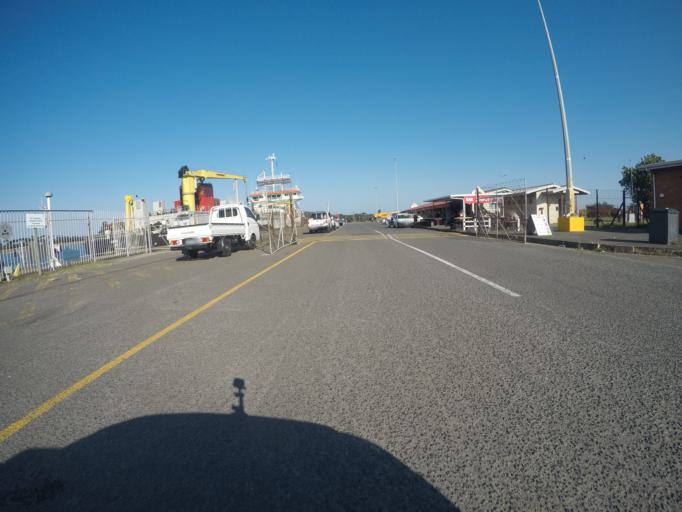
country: ZA
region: KwaZulu-Natal
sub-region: uThungulu District Municipality
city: Richards Bay
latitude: -28.7955
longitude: 32.0782
